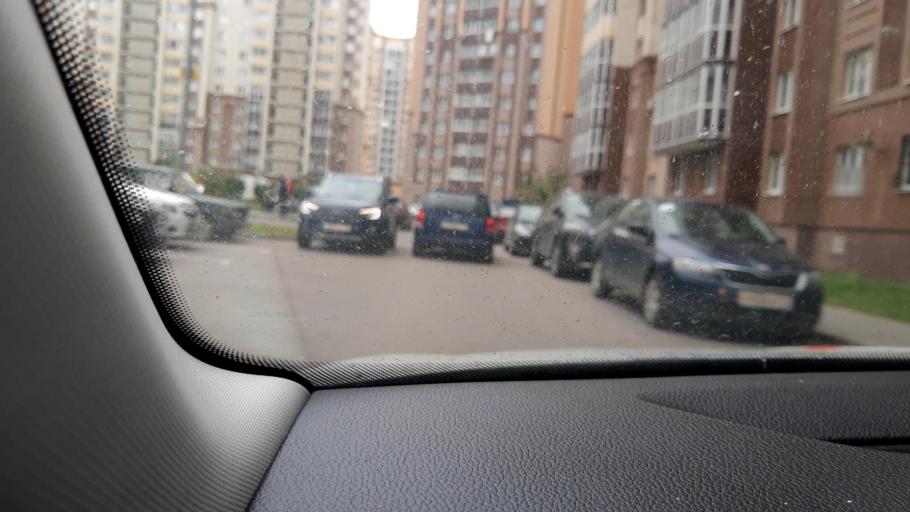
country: RU
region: Moskovskaya
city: Vostryakovo
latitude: 55.3998
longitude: 37.7729
